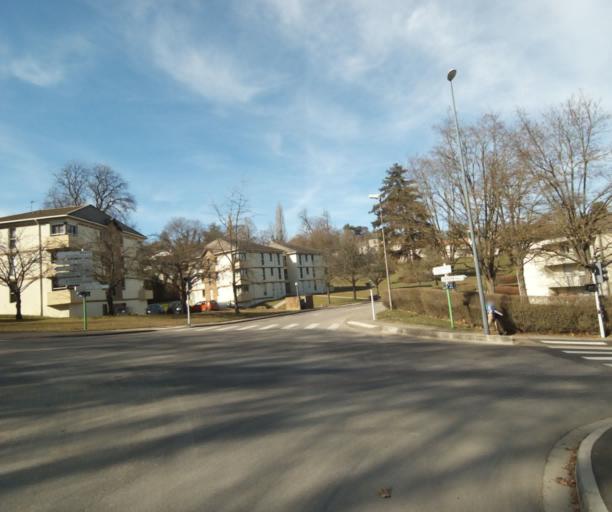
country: FR
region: Lorraine
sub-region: Departement de Meurthe-et-Moselle
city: Villers-les-Nancy
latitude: 48.6683
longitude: 6.1477
